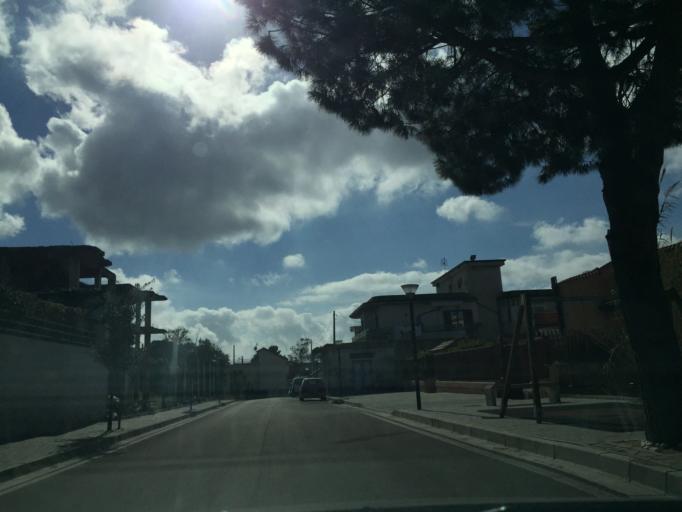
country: IT
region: Campania
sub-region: Provincia di Napoli
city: Pollena Trocchia
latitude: 40.8520
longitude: 14.3811
